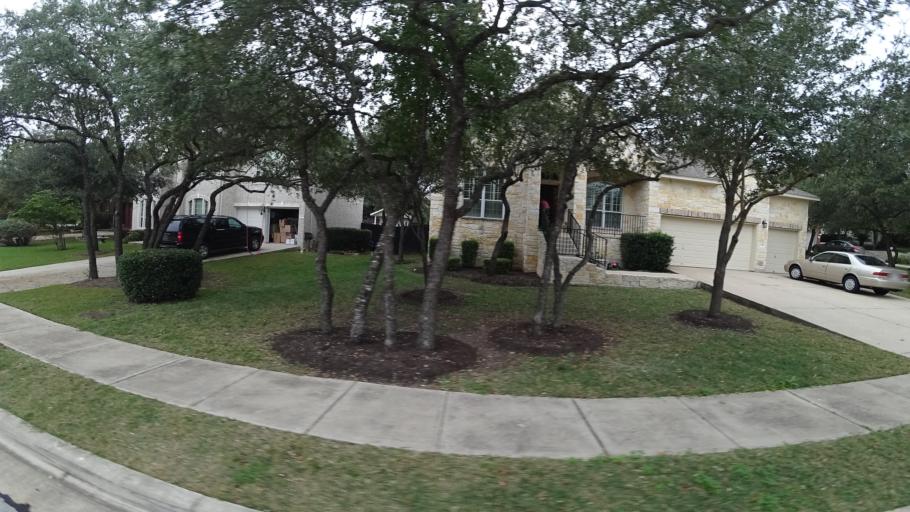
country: US
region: Texas
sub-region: Travis County
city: Bee Cave
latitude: 30.3570
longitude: -97.9051
